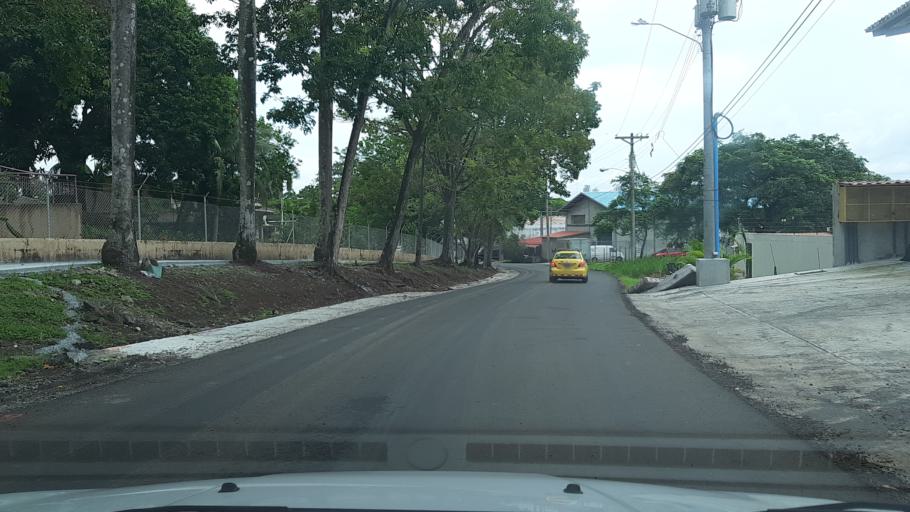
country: PA
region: Panama
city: San Miguelito
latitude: 9.0301
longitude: -79.4802
